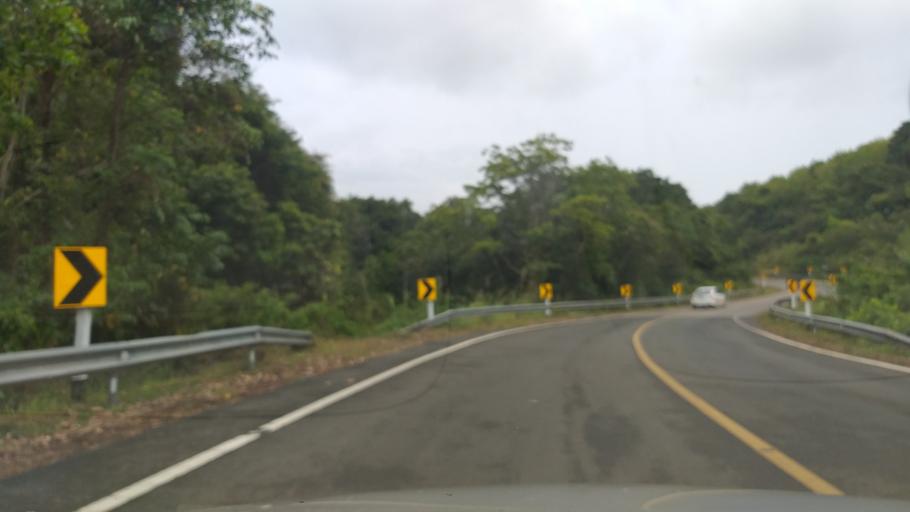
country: TH
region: Trat
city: Laem Ngop
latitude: 12.2009
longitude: 102.2887
